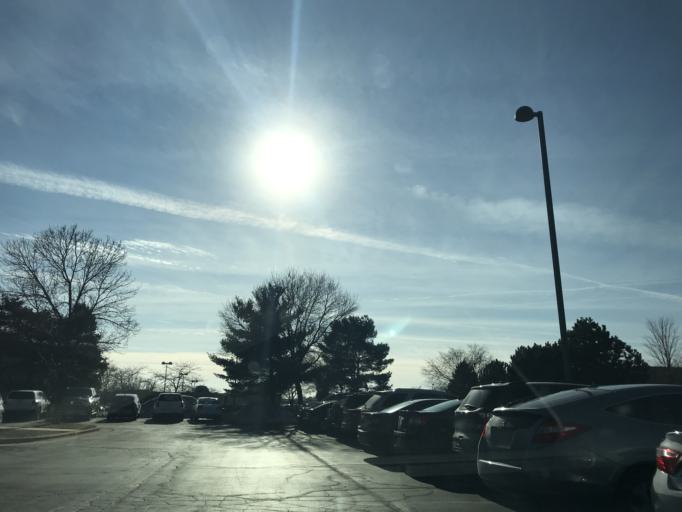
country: US
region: Wisconsin
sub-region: Dane County
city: Sun Prairie
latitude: 43.1495
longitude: -89.2915
